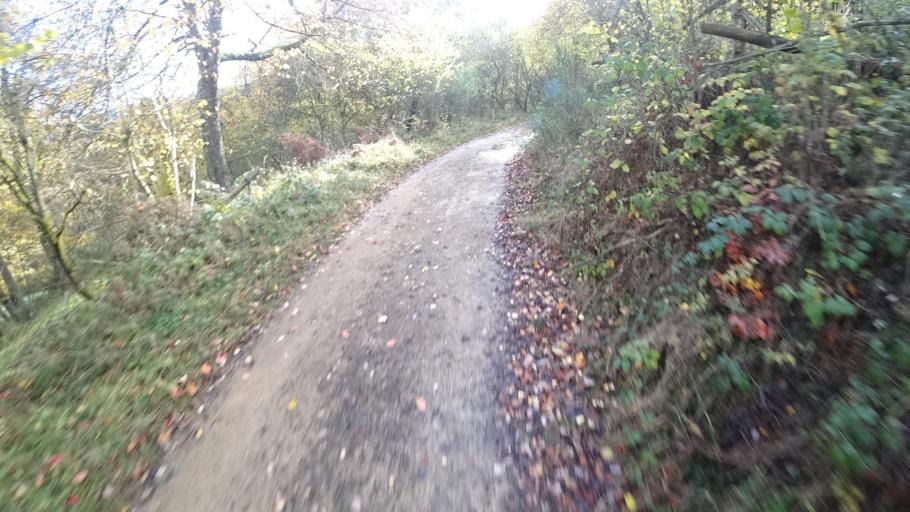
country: DE
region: Rheinland-Pfalz
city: Lind
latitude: 50.4885
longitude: 6.9405
